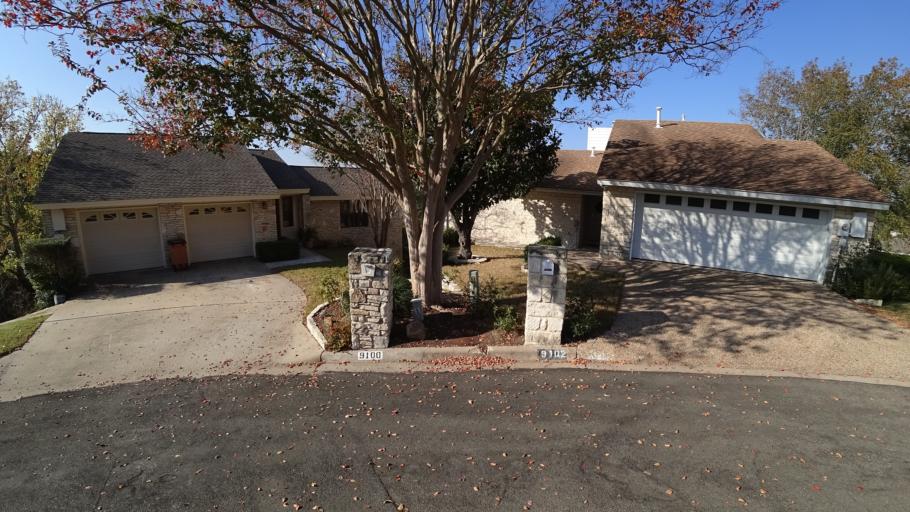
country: US
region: Texas
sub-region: Williamson County
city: Jollyville
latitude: 30.3920
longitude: -97.7621
